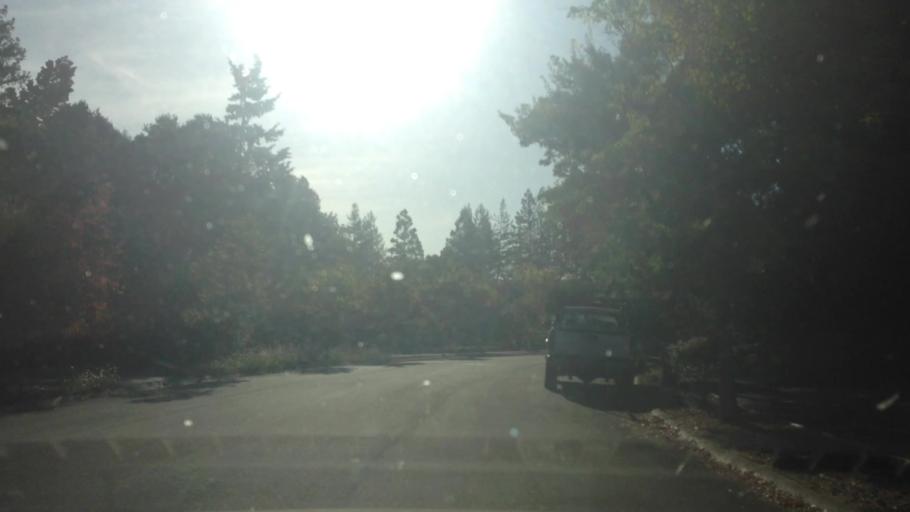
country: US
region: California
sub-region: Santa Clara County
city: Stanford
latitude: 37.4195
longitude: -122.1616
